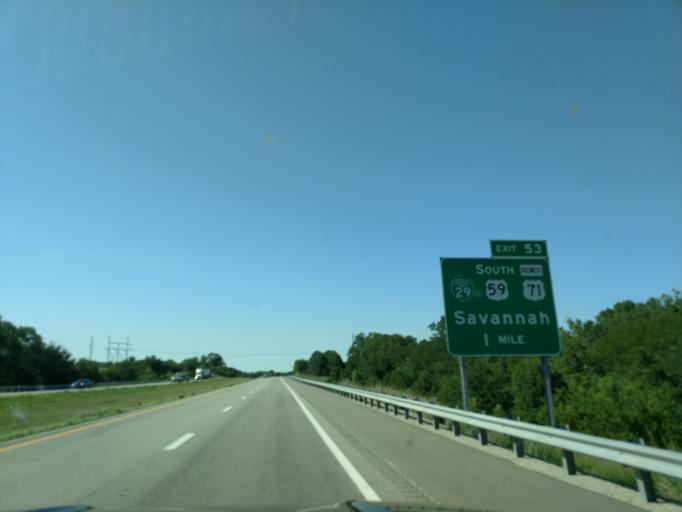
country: US
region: Missouri
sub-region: Andrew County
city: Country Club Village
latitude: 39.8409
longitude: -94.8051
